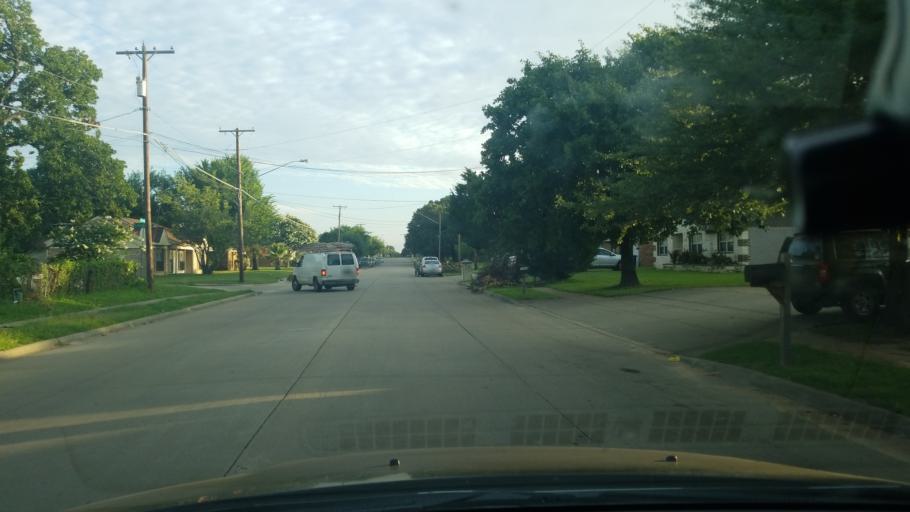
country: US
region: Texas
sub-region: Dallas County
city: Balch Springs
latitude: 32.7364
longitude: -96.6398
